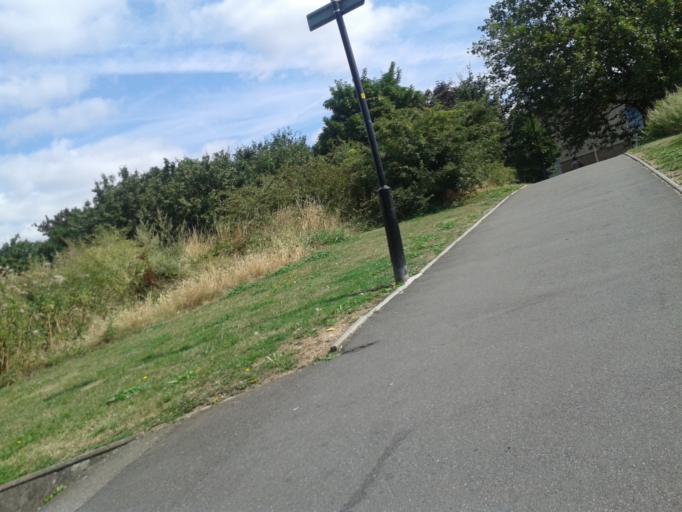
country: GB
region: England
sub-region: Greater London
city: Camberwell
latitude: 51.4829
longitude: -0.0729
